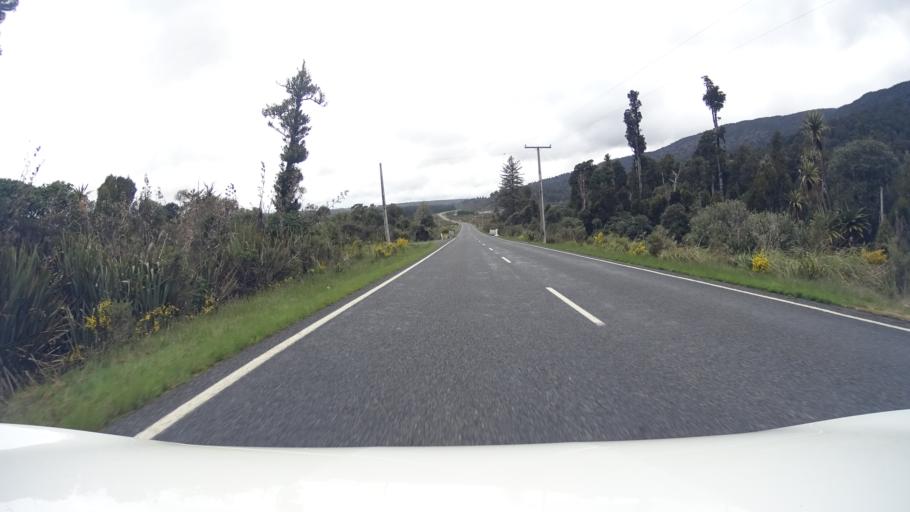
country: NZ
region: Manawatu-Wanganui
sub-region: Ruapehu District
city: Waiouru
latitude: -39.2356
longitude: 175.3919
